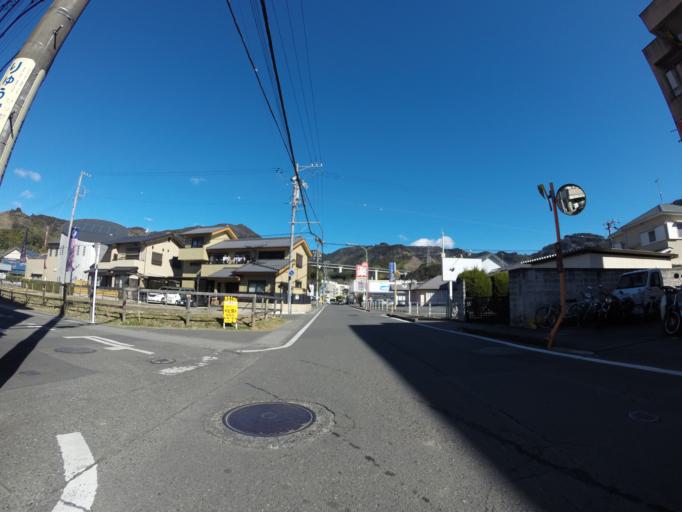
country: JP
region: Shizuoka
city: Shizuoka-shi
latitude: 35.0368
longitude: 138.3968
